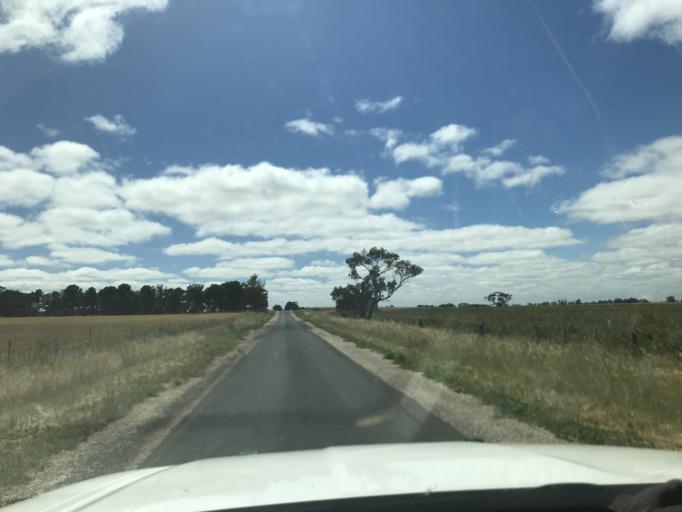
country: AU
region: South Australia
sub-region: Tatiara
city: Bordertown
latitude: -36.2803
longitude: 141.1333
